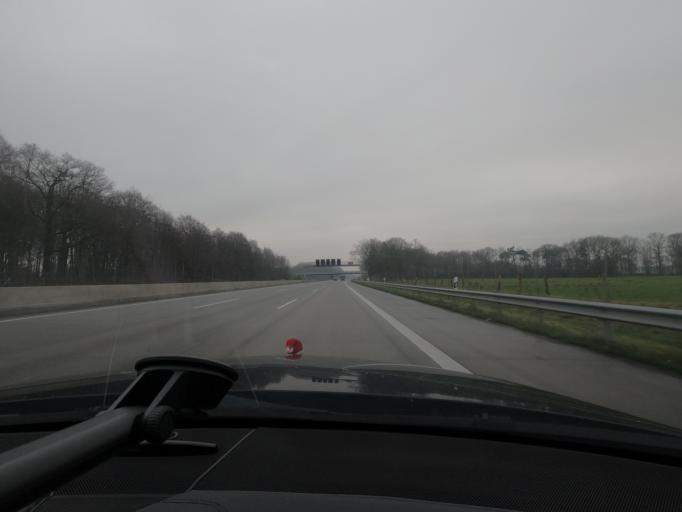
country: DE
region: Schleswig-Holstein
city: Norderstedt
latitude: 53.6915
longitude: 9.9455
